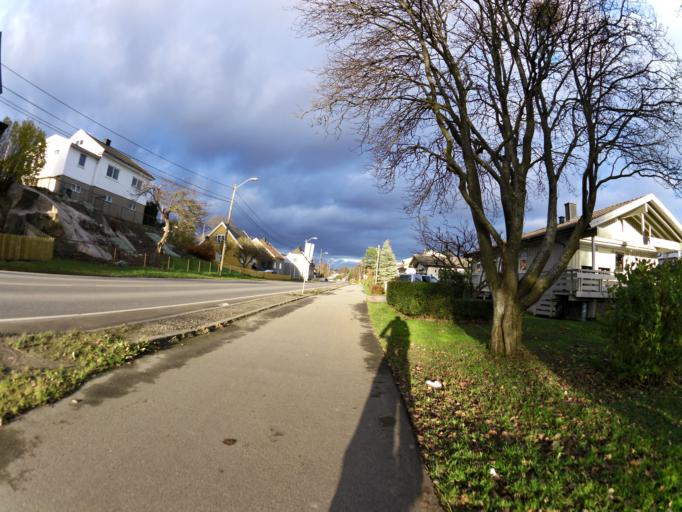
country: NO
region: Ostfold
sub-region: Fredrikstad
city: Fredrikstad
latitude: 59.2191
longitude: 10.9075
